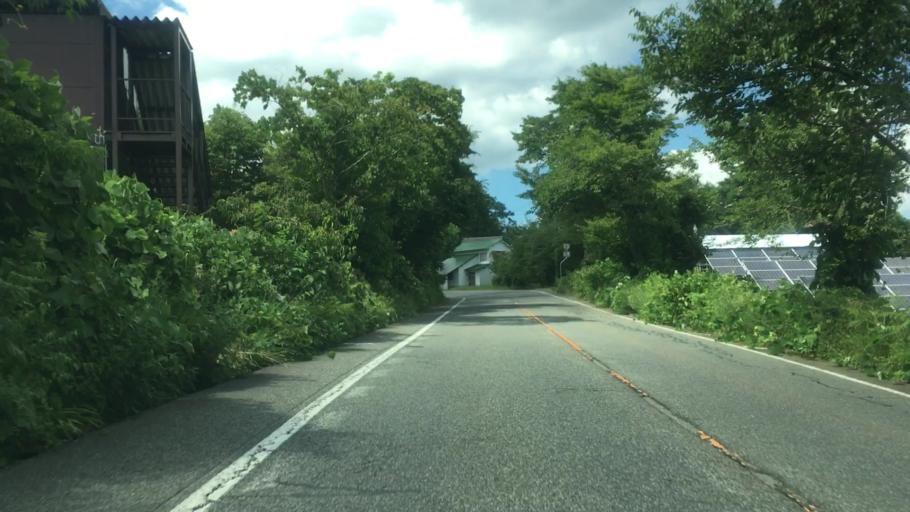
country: JP
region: Hyogo
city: Toyooka
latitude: 35.4918
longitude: 134.6893
